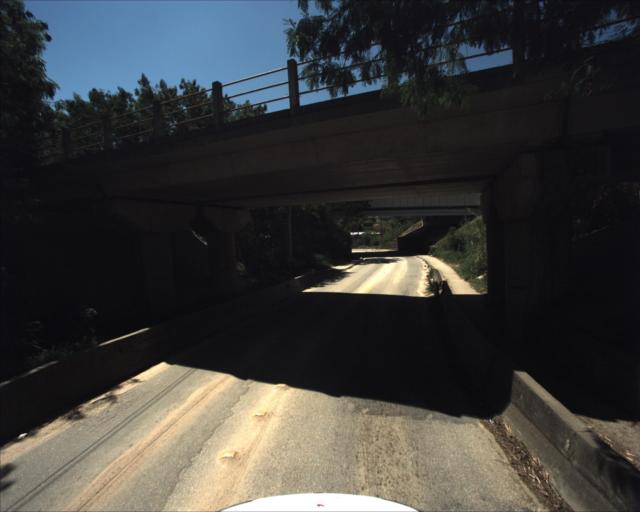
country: BR
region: Sao Paulo
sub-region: Votorantim
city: Votorantim
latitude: -23.5032
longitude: -47.3708
